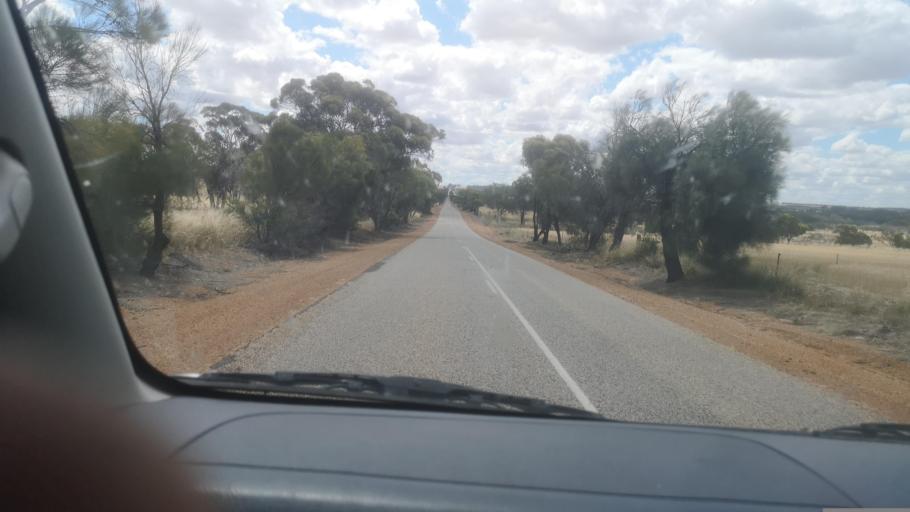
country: AU
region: Western Australia
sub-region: Beverley
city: Beverley
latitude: -31.9883
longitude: 117.0990
